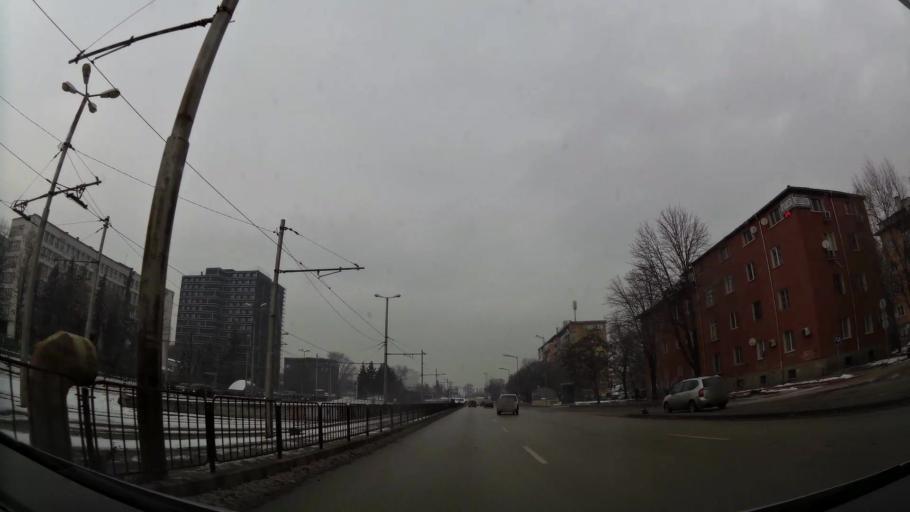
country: BG
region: Sofia-Capital
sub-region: Stolichna Obshtina
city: Sofia
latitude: 42.7141
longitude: 23.3135
